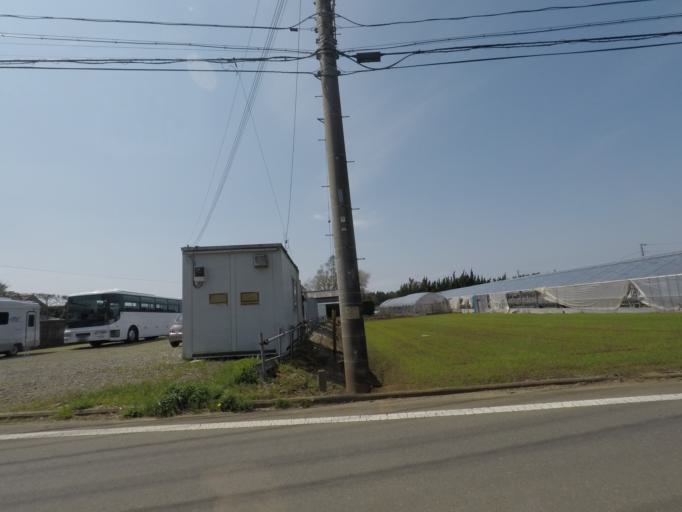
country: JP
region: Chiba
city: Yachimata
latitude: 35.7096
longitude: 140.4056
